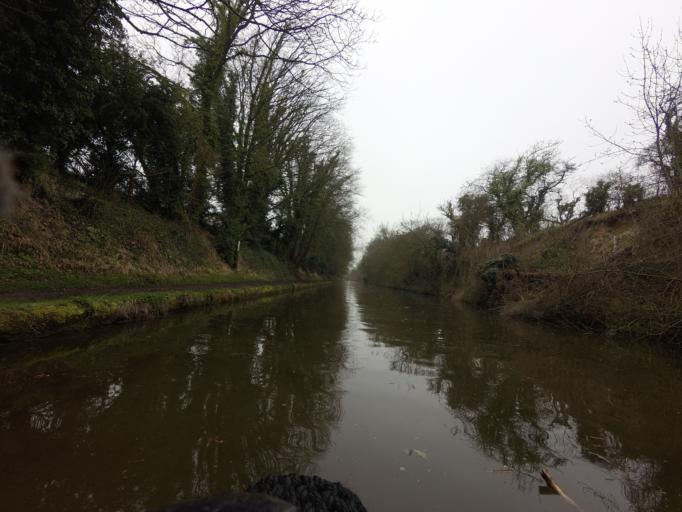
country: GB
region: England
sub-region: Hertfordshire
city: Tring
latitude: 51.7962
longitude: -0.6201
